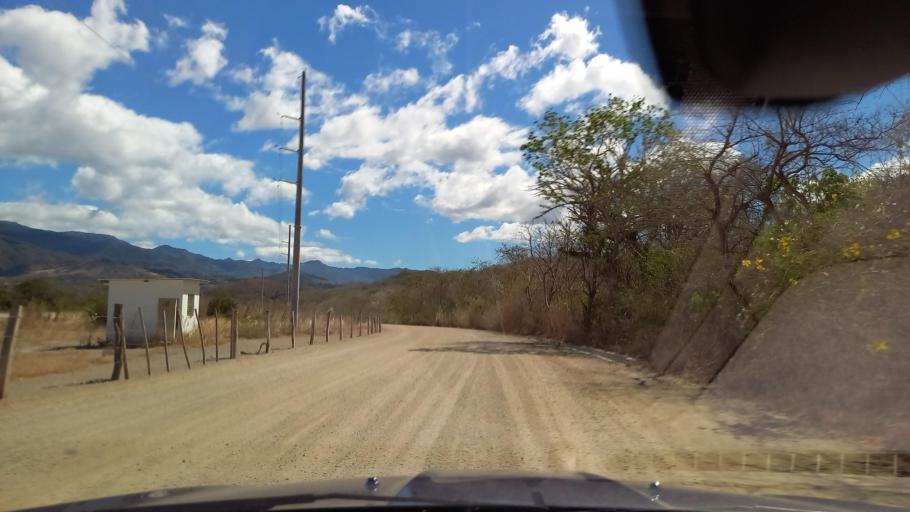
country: SV
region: Santa Ana
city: Metapan
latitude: 14.3606
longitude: -89.4749
